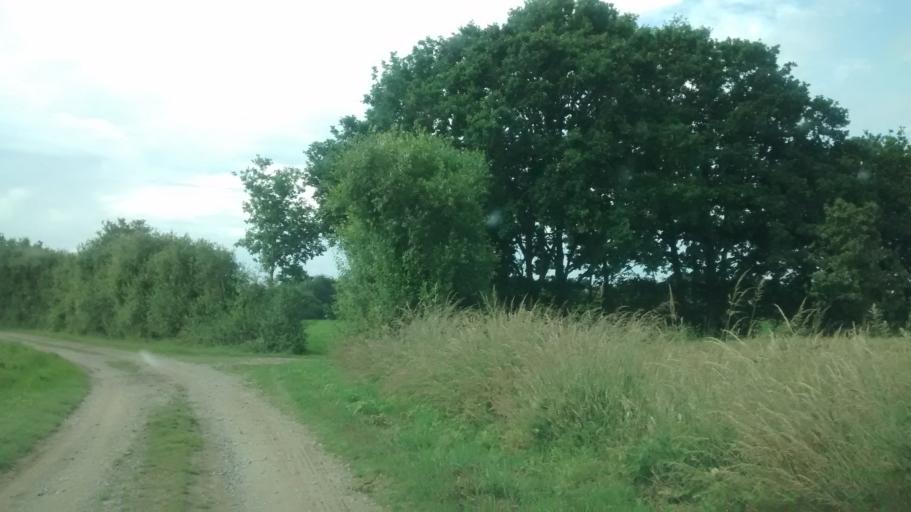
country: FR
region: Brittany
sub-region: Departement d'Ille-et-Vilaine
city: Plechatel
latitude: 47.8343
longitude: -1.7467
